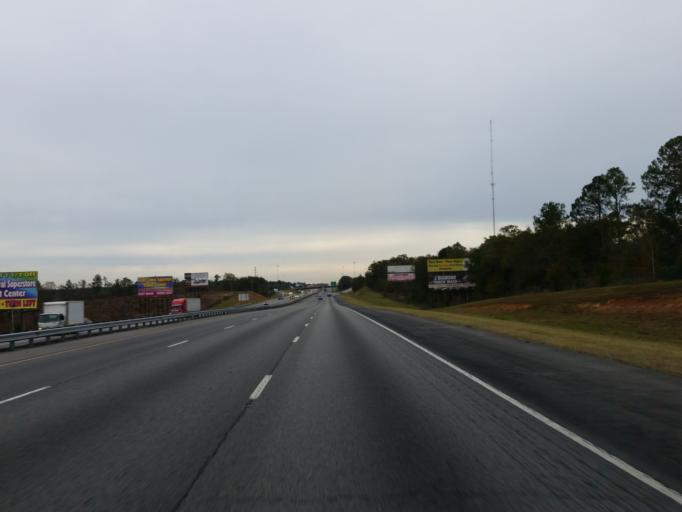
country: US
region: Georgia
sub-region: Crisp County
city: Cordele
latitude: 31.9160
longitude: -83.7416
